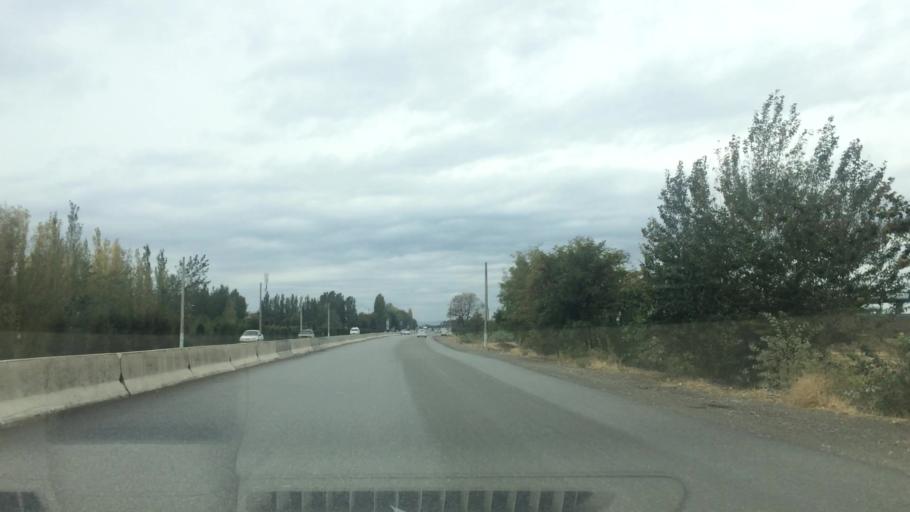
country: UZ
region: Jizzax
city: Jizzax
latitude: 40.0153
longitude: 67.6058
